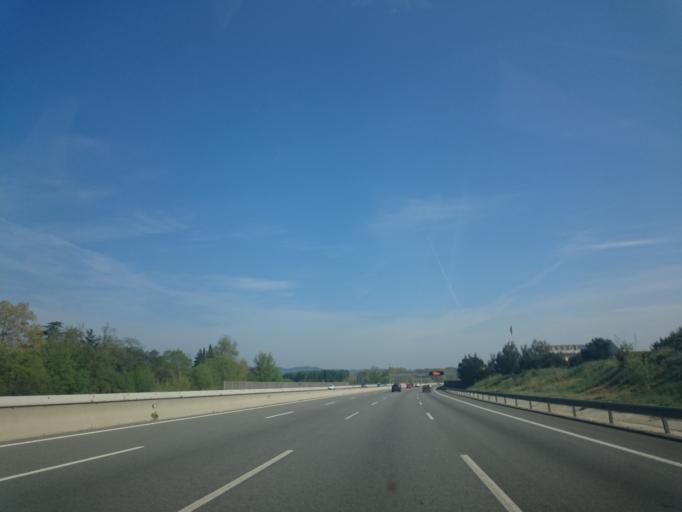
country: ES
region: Catalonia
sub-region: Provincia de Girona
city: Salt
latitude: 41.9729
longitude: 2.7784
